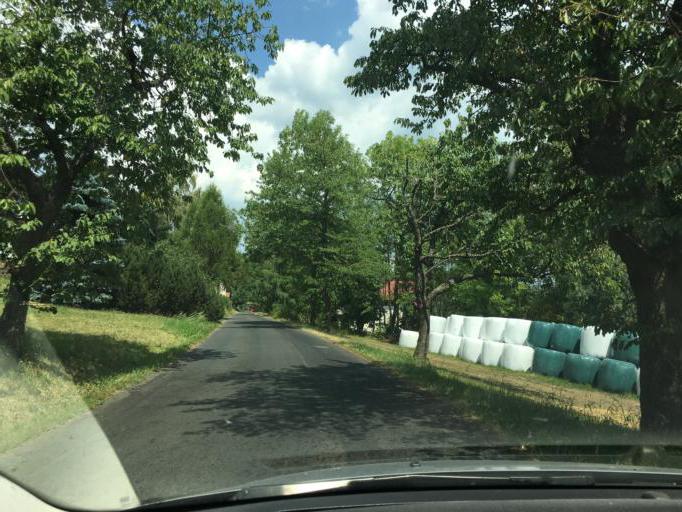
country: CZ
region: Liberecky
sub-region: Okres Semily
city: Ponikla
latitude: 50.6791
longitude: 15.4904
